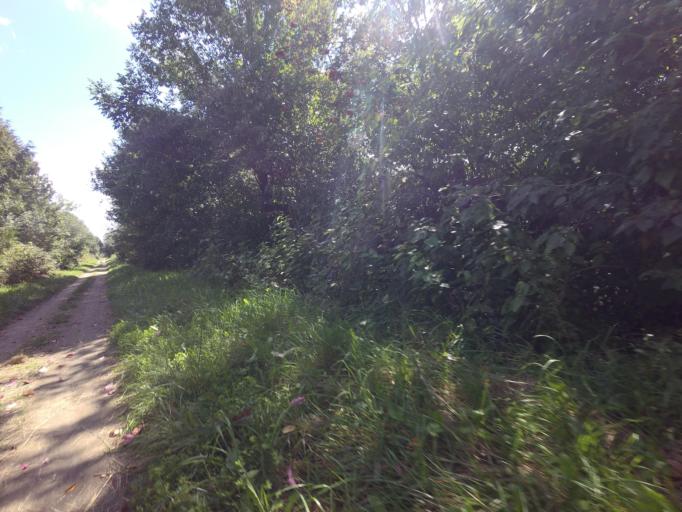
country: CA
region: Ontario
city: Orangeville
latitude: 43.7927
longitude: -80.3004
